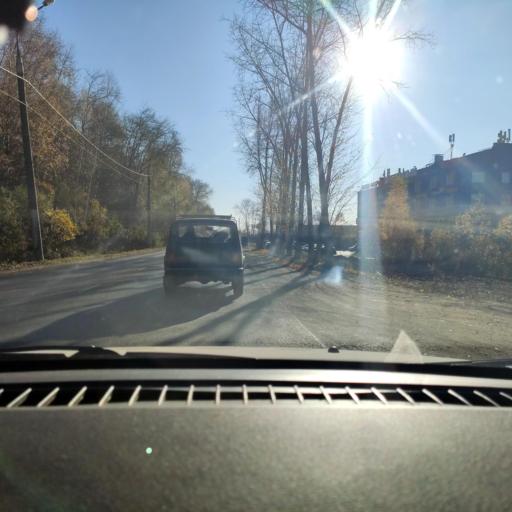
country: RU
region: Perm
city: Perm
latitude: 58.0689
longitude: 56.3464
